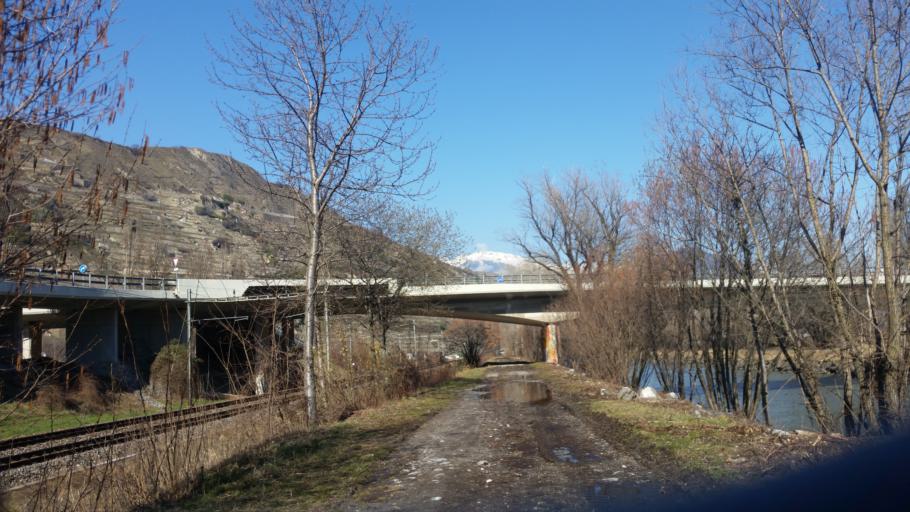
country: CH
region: Valais
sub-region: Sion District
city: Sitten
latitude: 46.2374
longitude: 7.3732
